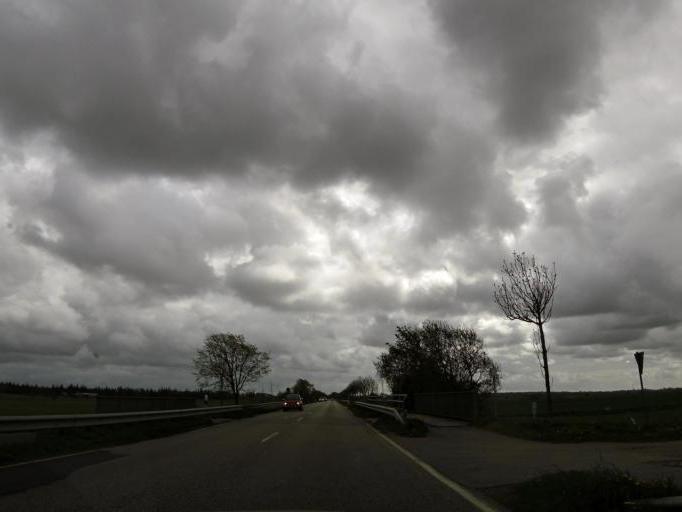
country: DE
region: Schleswig-Holstein
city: Suderlugum
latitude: 54.8964
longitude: 8.9123
